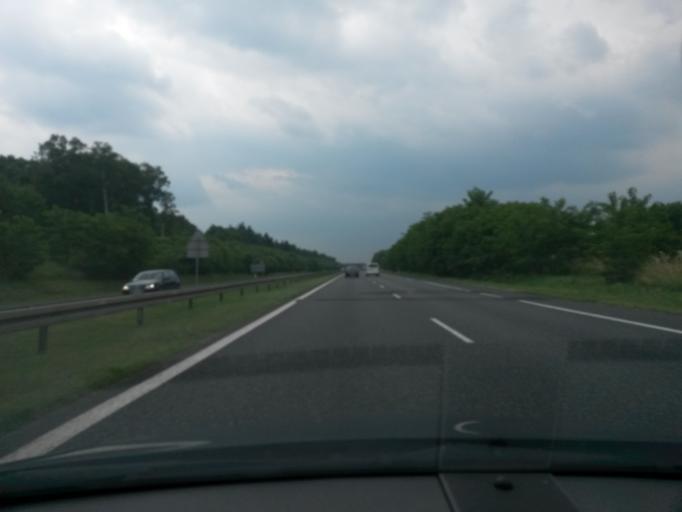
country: PL
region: Lodz Voivodeship
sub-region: Powiat radomszczanski
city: Radomsko
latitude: 51.0757
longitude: 19.3701
